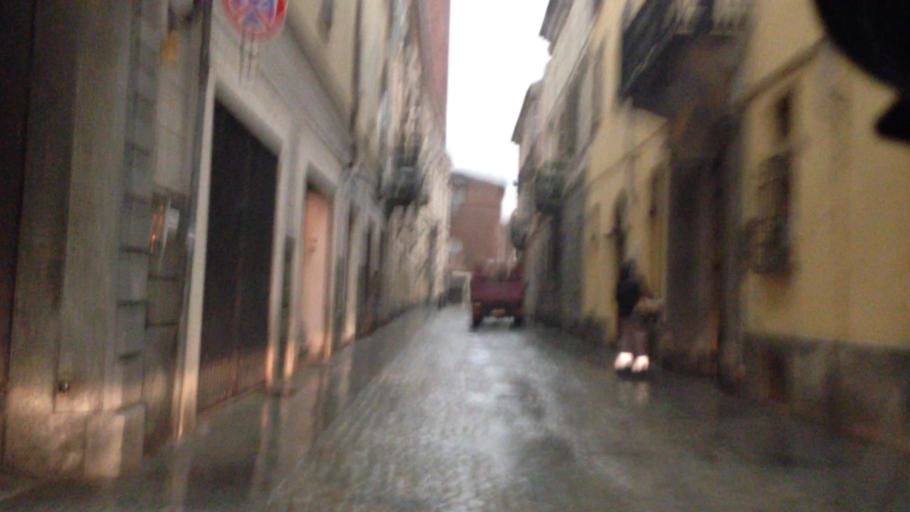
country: IT
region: Piedmont
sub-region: Provincia di Asti
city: Asti
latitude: 44.8982
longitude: 8.2022
